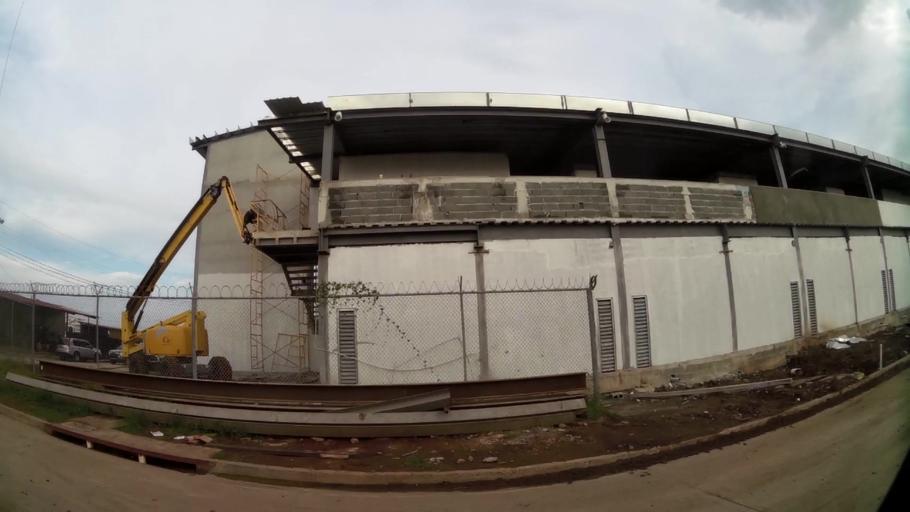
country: PA
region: Panama
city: Tocumen
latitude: 9.0924
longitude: -79.3872
